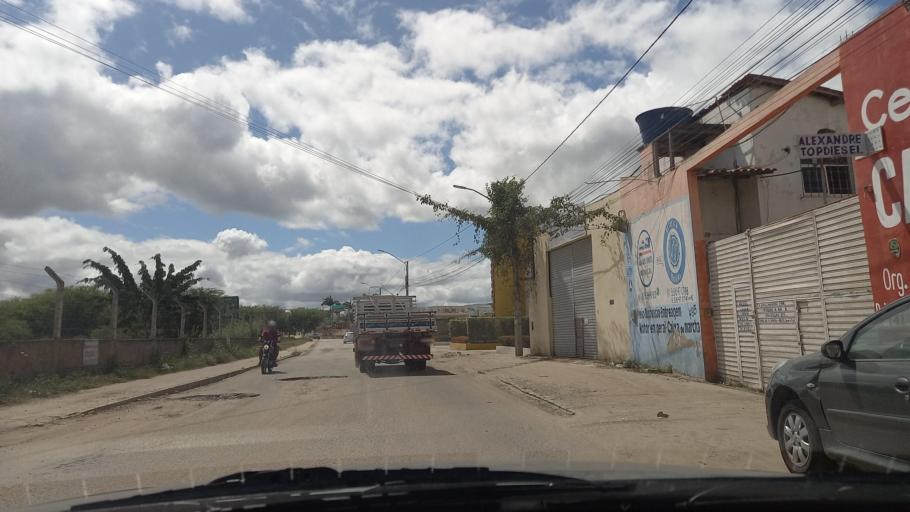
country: BR
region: Pernambuco
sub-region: Caruaru
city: Caruaru
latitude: -8.2628
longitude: -35.9593
